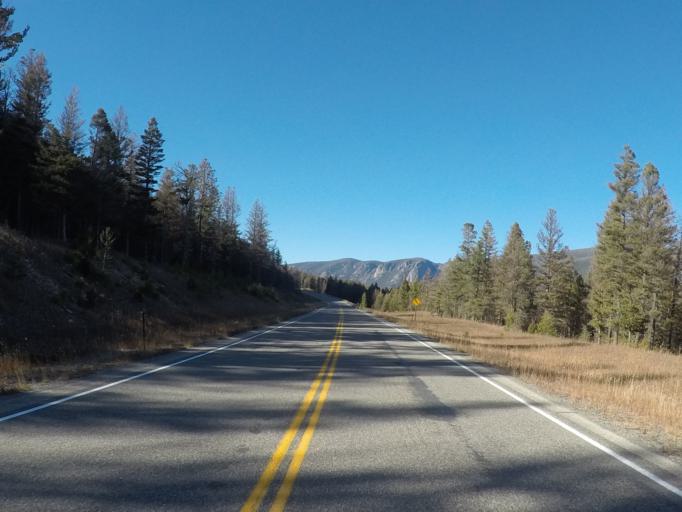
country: US
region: Montana
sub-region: Carbon County
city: Red Lodge
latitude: 44.8189
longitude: -109.4634
